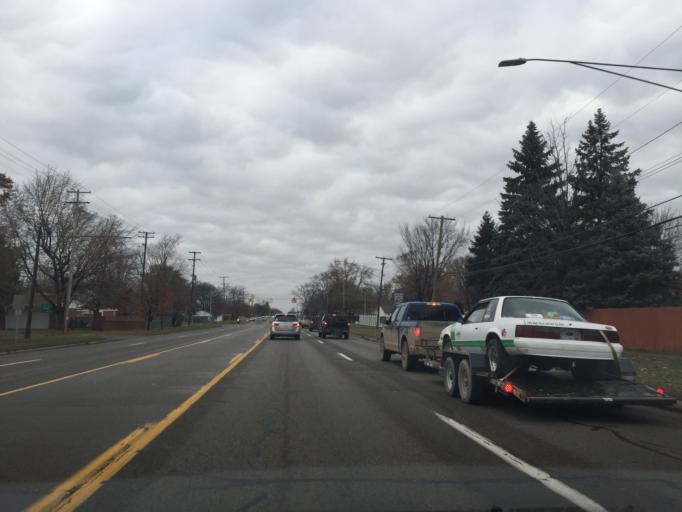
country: US
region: Michigan
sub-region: Wayne County
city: Livonia
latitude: 42.3895
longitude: -83.3340
